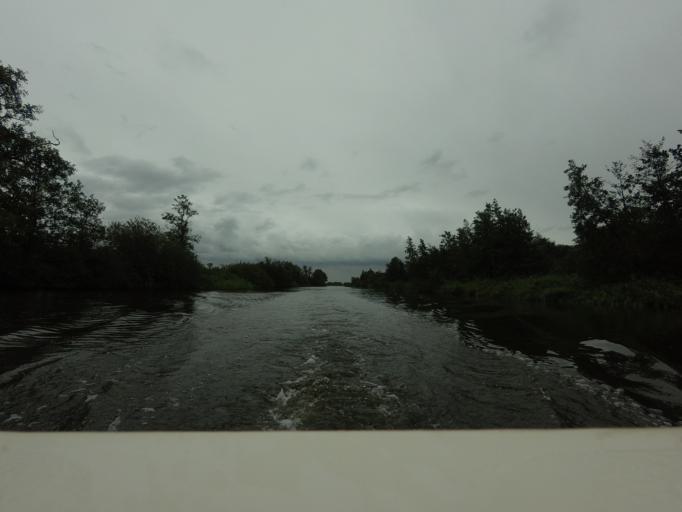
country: NL
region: Friesland
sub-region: Gemeente Boarnsterhim
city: Warten
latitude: 53.1190
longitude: 5.9312
